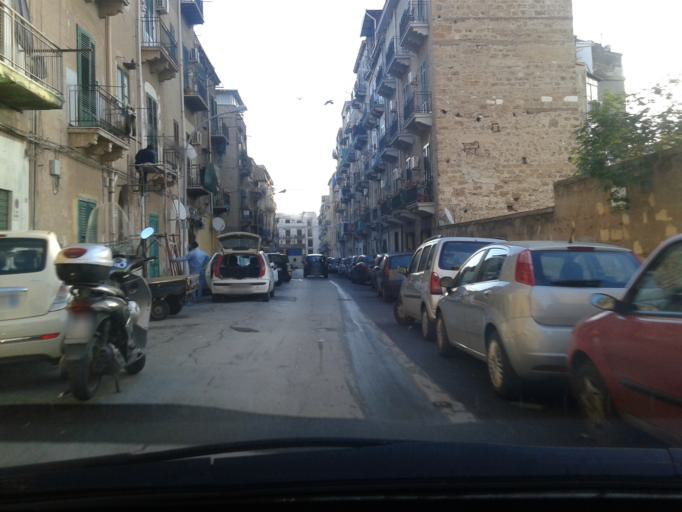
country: IT
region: Sicily
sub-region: Palermo
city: Palermo
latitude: 38.1135
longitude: 13.3455
